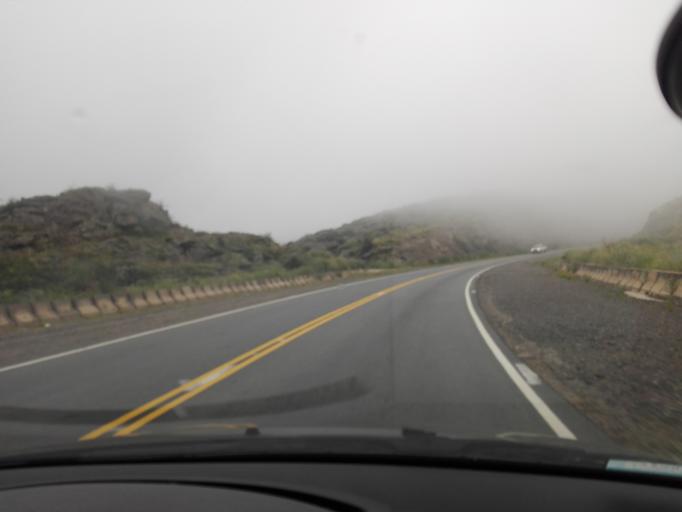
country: AR
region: Cordoba
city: Cuesta Blanca
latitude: -31.6002
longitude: -64.7095
